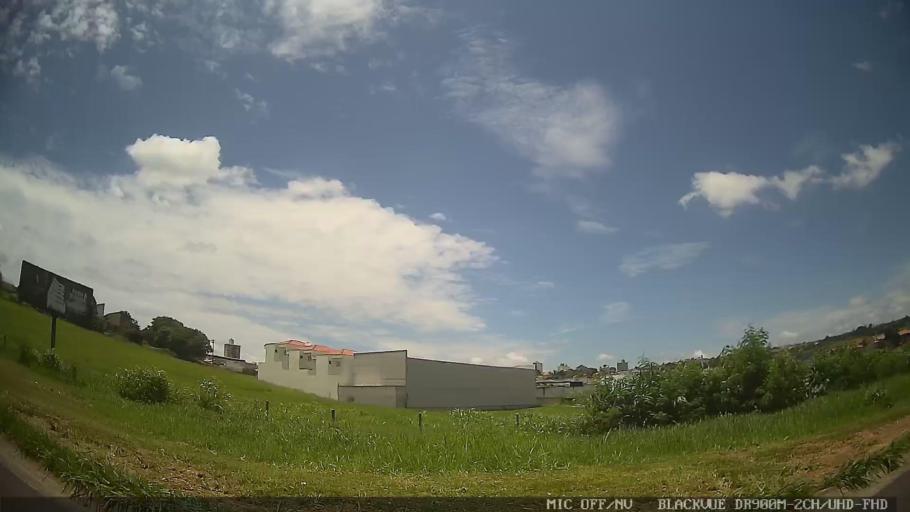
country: BR
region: Sao Paulo
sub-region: Laranjal Paulista
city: Laranjal Paulista
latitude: -23.0406
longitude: -47.8397
